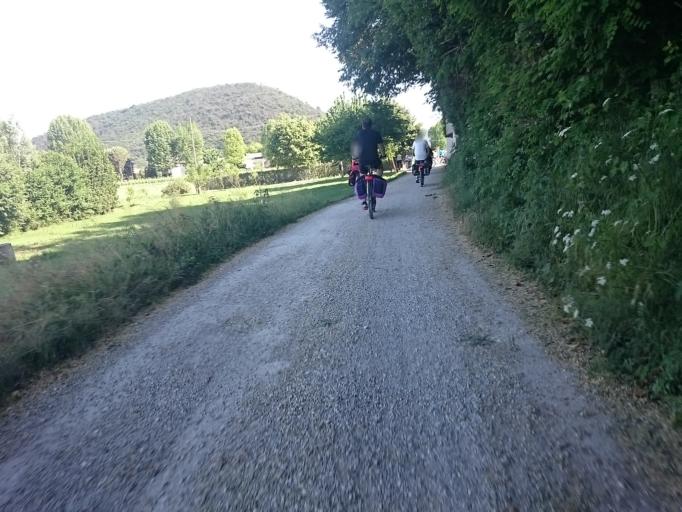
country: IT
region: Veneto
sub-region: Provincia di Padova
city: San Biagio
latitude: 45.3595
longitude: 11.7428
